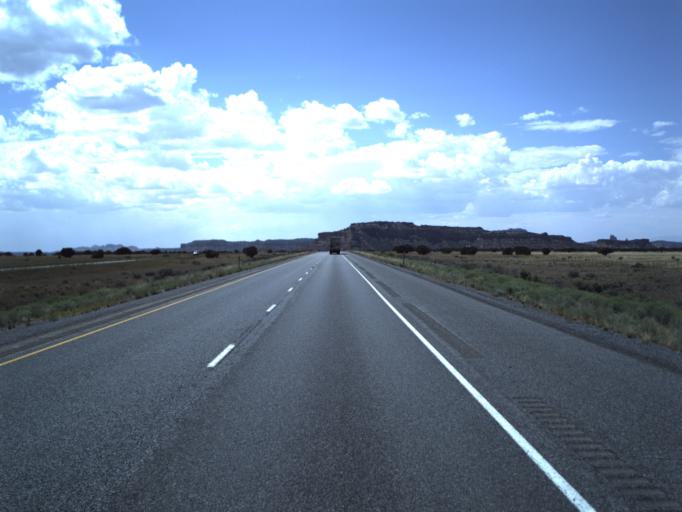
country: US
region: Utah
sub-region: Emery County
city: Castle Dale
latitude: 38.8926
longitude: -110.6316
